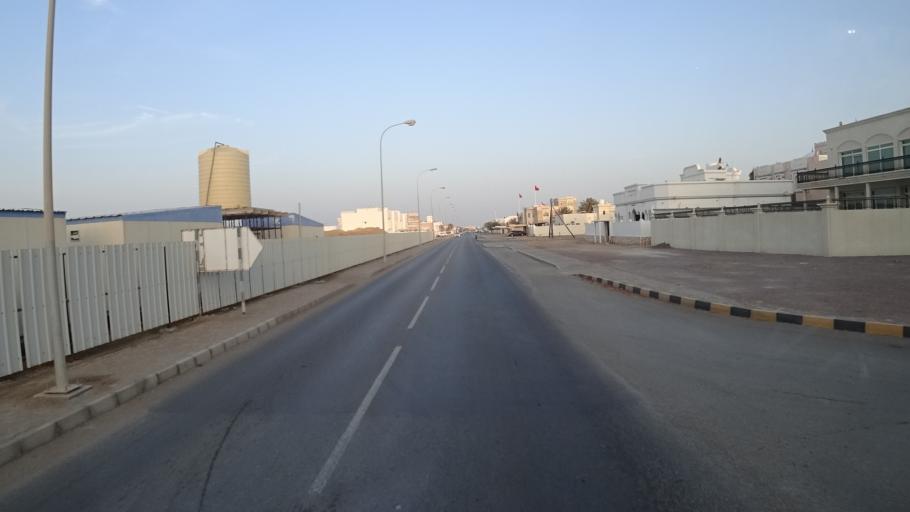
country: OM
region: Ash Sharqiyah
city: Sur
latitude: 22.5949
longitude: 59.4940
